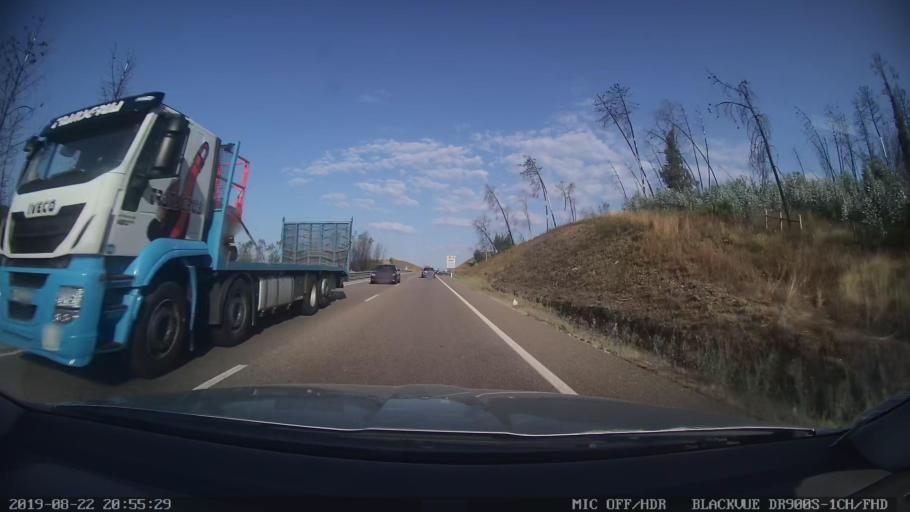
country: PT
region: Castelo Branco
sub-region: Serta
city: Serta
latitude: 39.7807
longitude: -8.0343
